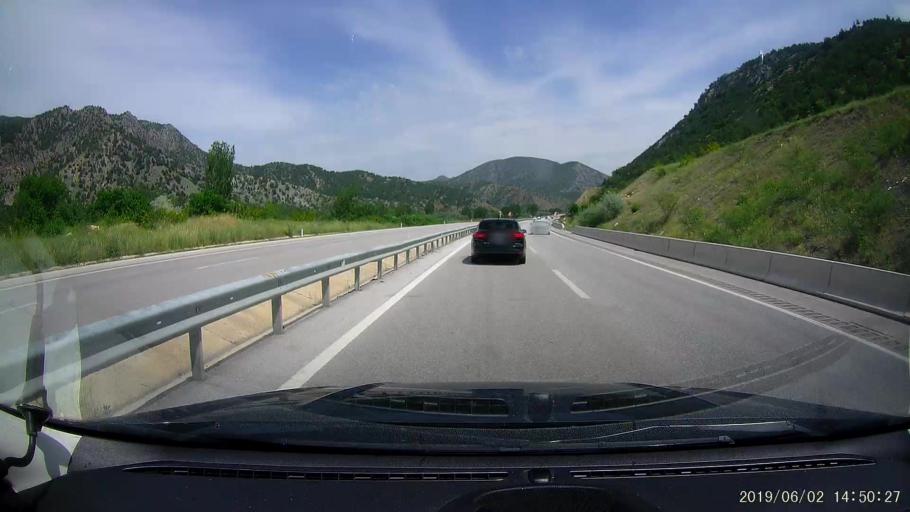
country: TR
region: Corum
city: Kargi
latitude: 41.0716
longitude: 34.5197
